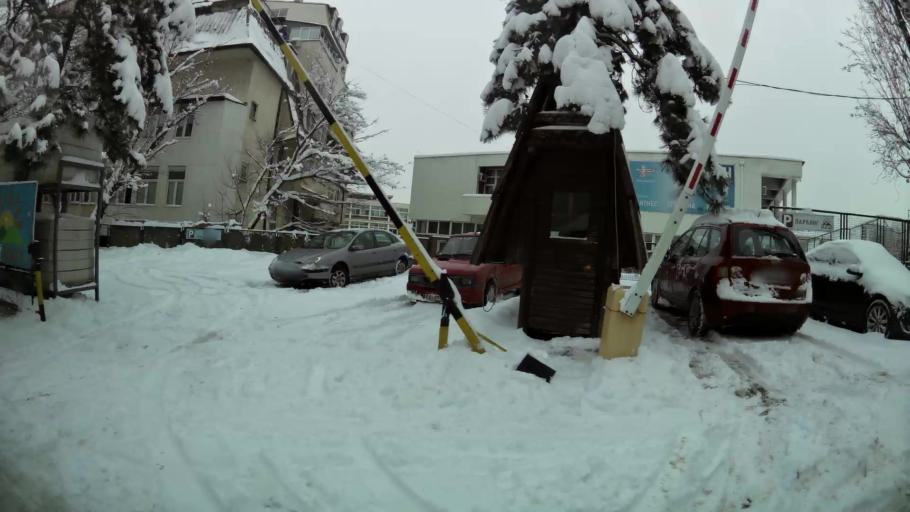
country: RS
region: Central Serbia
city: Belgrade
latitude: 44.8128
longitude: 20.4825
